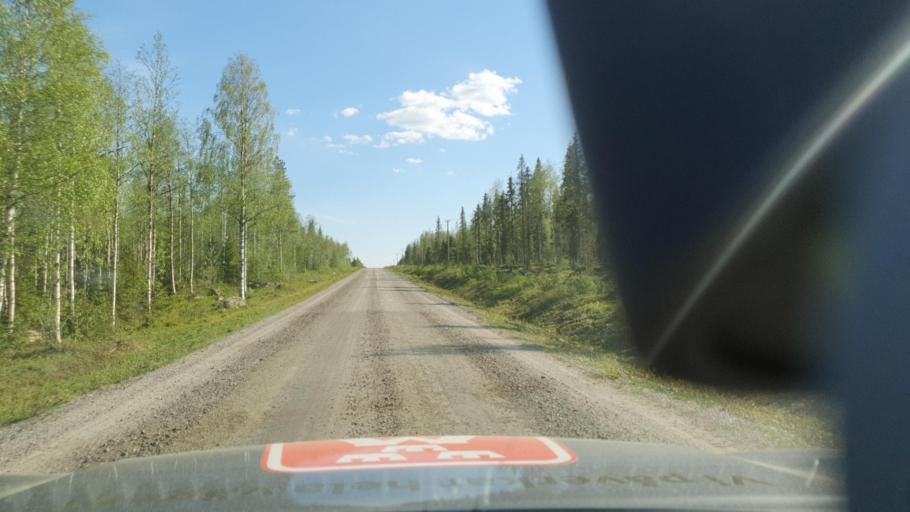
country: SE
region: Norrbotten
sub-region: Bodens Kommun
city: Boden
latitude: 66.5096
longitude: 21.9089
